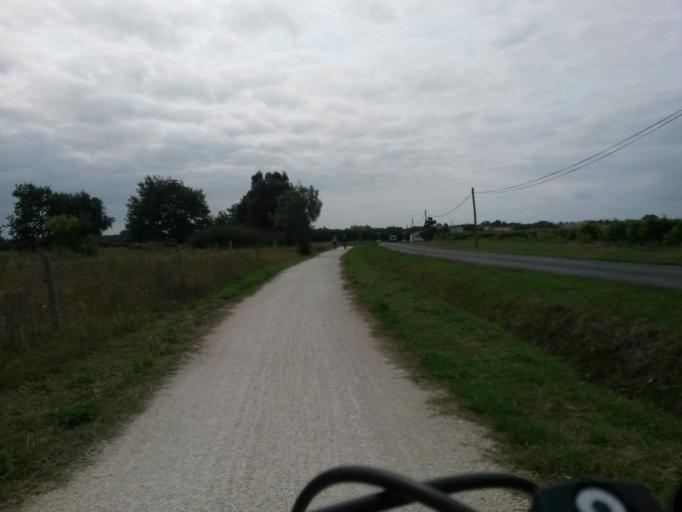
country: FR
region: Poitou-Charentes
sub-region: Departement de la Charente-Maritime
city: Dolus-d'Oleron
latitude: 45.8853
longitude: -1.2413
